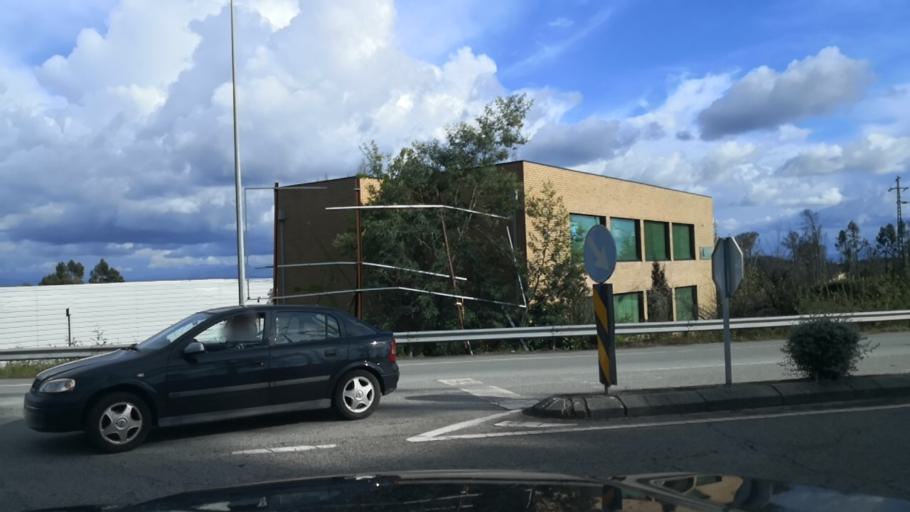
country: PT
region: Viseu
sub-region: Concelho de Tondela
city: Tondela
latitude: 40.4990
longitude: -8.0832
